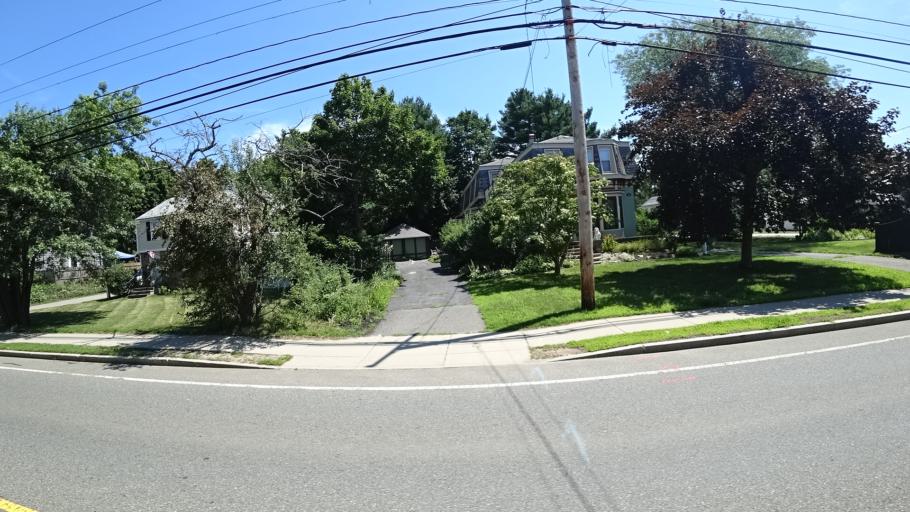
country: US
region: Massachusetts
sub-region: Norfolk County
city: Dedham
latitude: 42.2364
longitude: -71.1631
